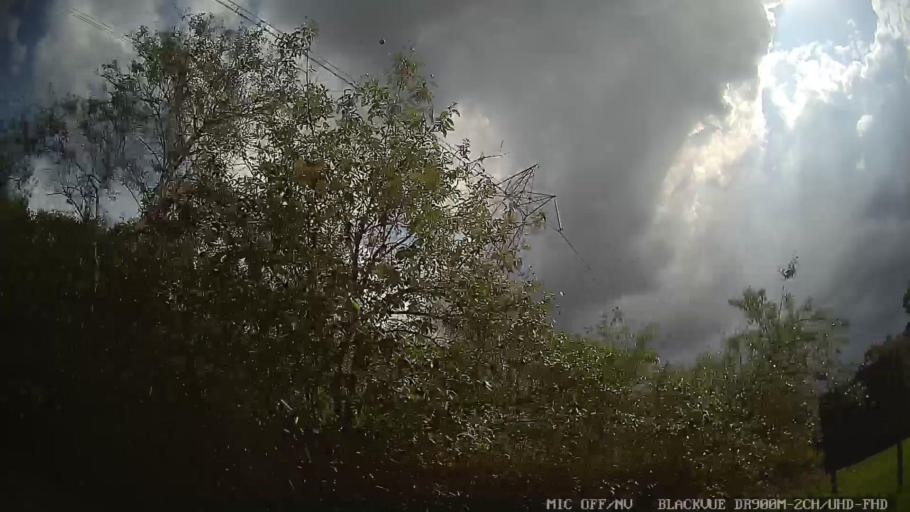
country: BR
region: Sao Paulo
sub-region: Louveira
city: Louveira
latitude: -23.0878
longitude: -46.9403
